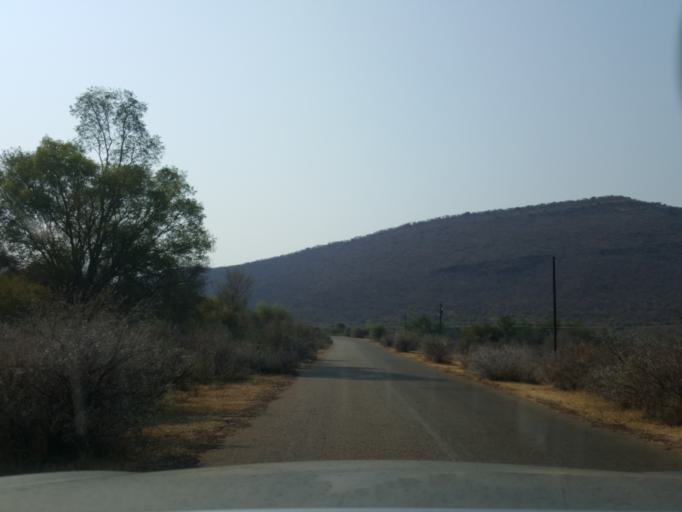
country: BW
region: South East
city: Lobatse
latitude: -25.3283
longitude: 25.7766
